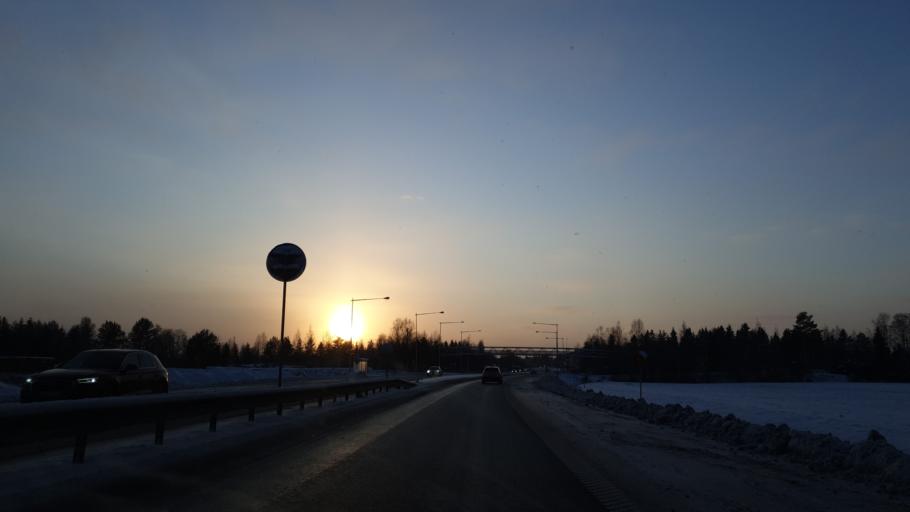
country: SE
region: Vaesterbotten
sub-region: Umea Kommun
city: Roback
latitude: 63.7792
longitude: 20.1911
